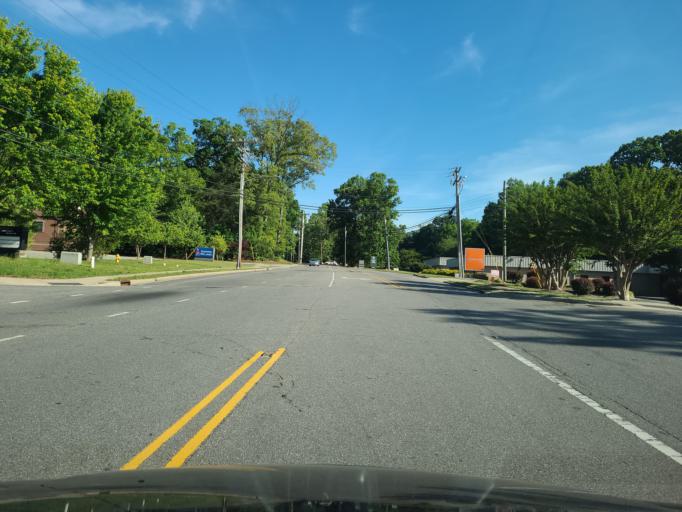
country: US
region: North Carolina
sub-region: Iredell County
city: Statesville
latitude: 35.8031
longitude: -80.8762
